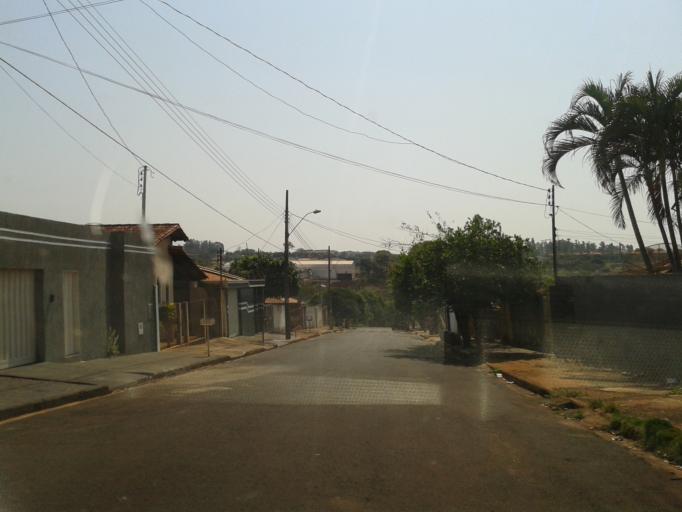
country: BR
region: Minas Gerais
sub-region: Ituiutaba
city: Ituiutaba
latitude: -18.9705
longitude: -49.4856
